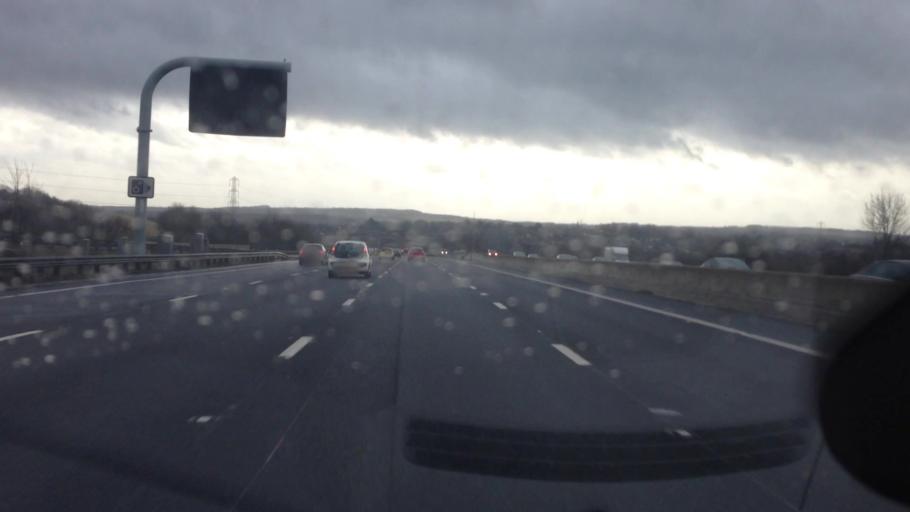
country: GB
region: England
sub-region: City and Borough of Wakefield
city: Horbury
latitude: 53.6811
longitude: -1.5543
